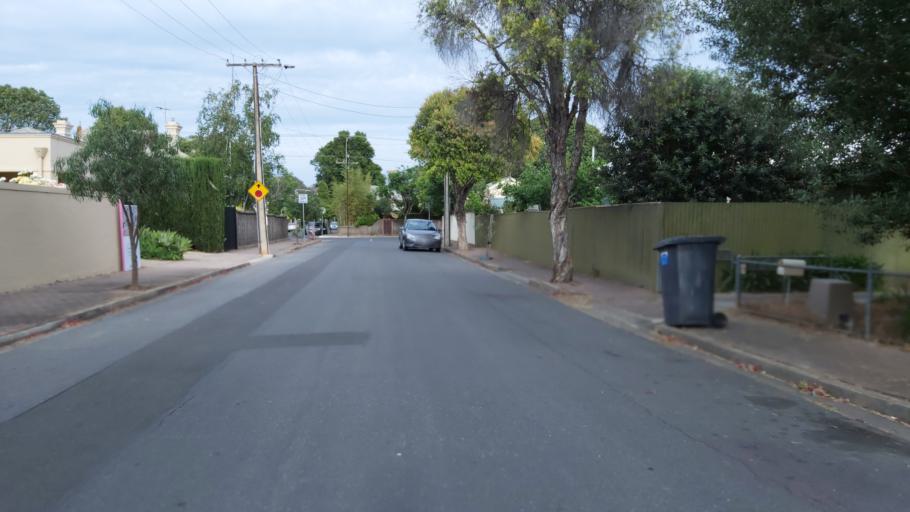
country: AU
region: South Australia
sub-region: Unley
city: Unley
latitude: -34.9528
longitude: 138.5979
